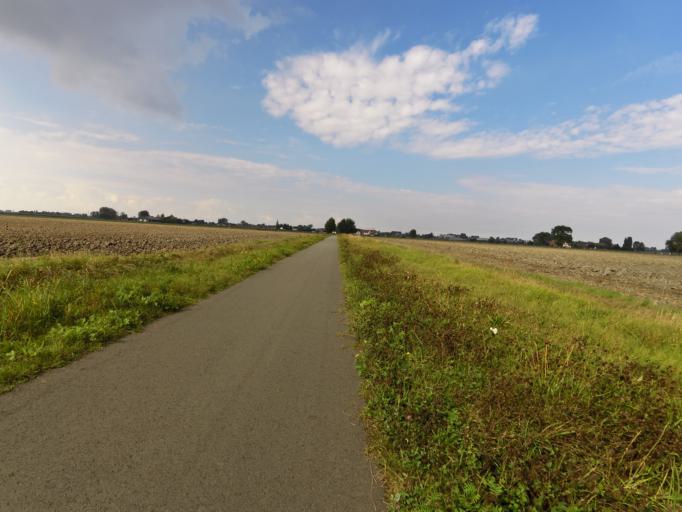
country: BE
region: Flanders
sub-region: Provincie West-Vlaanderen
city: Gistel
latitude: 51.1673
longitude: 2.9480
